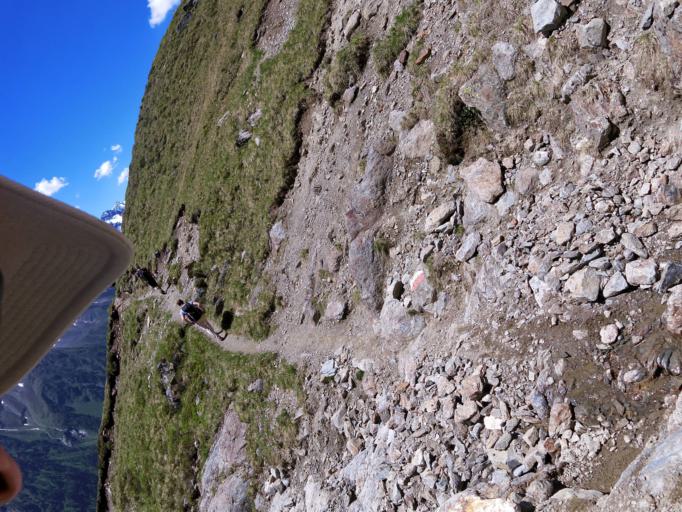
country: AT
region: Tyrol
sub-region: Politischer Bezirk Innsbruck Land
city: Neustift im Stubaital
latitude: 47.1321
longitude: 11.2340
